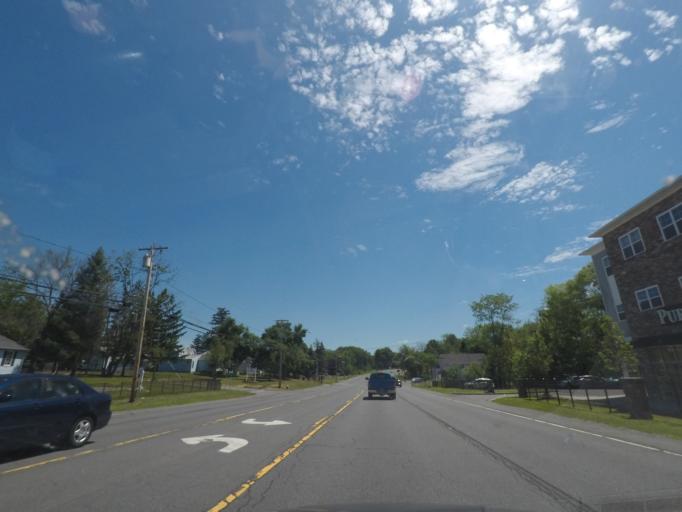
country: US
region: New York
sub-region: Albany County
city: Watervliet
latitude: 42.7427
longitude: -73.7437
